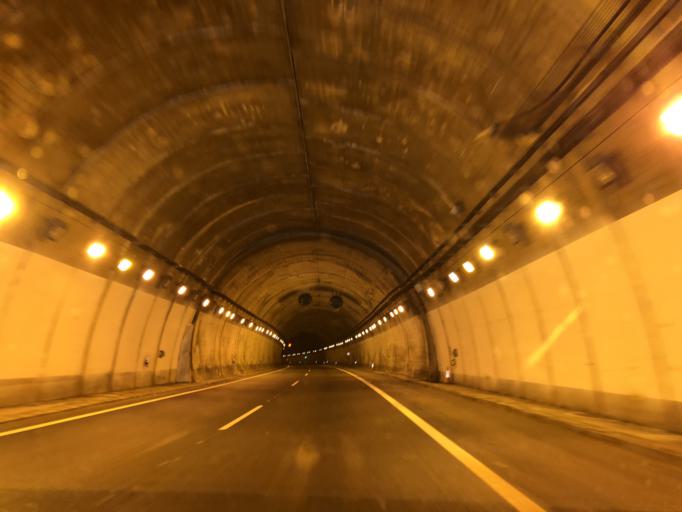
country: ES
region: Andalusia
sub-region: Provincia de Malaga
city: Manilva
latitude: 36.4014
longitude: -5.2419
